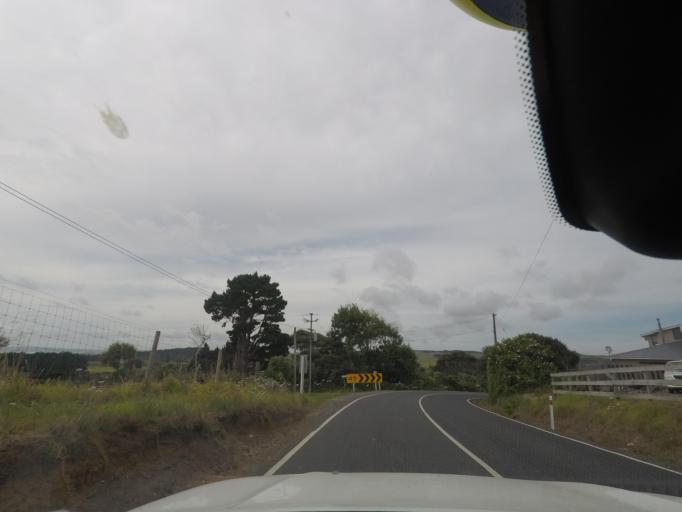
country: NZ
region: Auckland
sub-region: Auckland
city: Parakai
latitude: -36.5101
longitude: 174.2476
